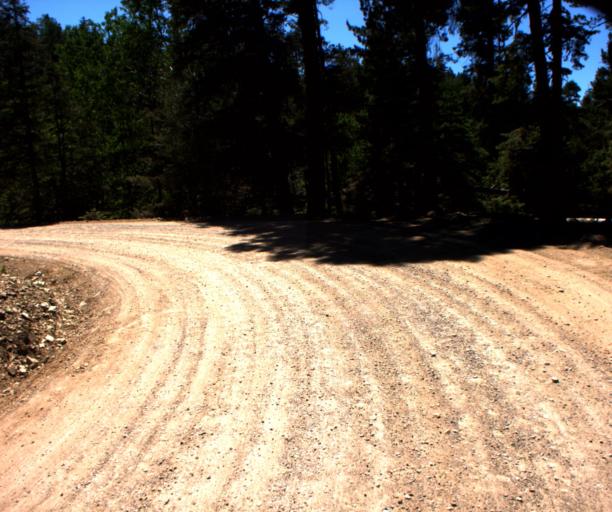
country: US
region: Arizona
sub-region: Graham County
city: Swift Trail Junction
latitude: 32.6746
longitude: -109.8873
